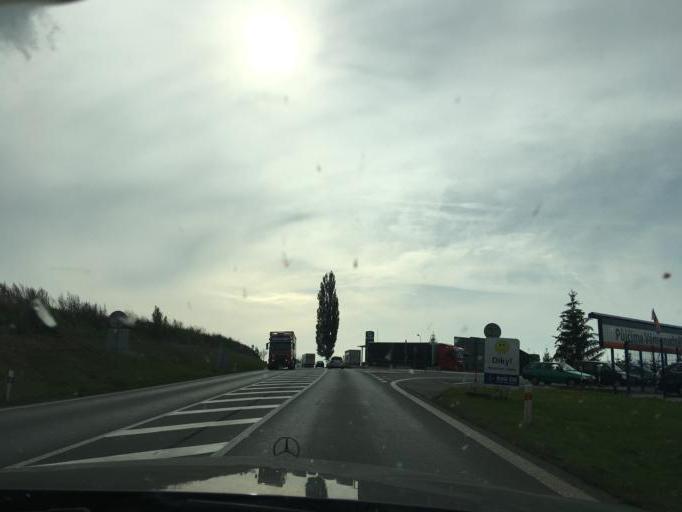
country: CZ
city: Predmerice nad Labem
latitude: 50.2877
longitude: 15.8269
